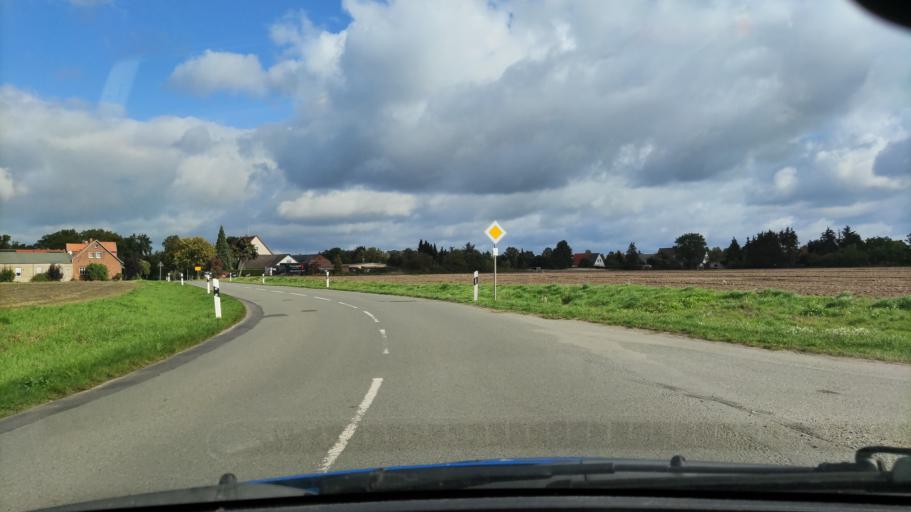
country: DE
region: Saxony-Anhalt
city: Salzwedel
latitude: 52.8532
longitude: 11.2065
